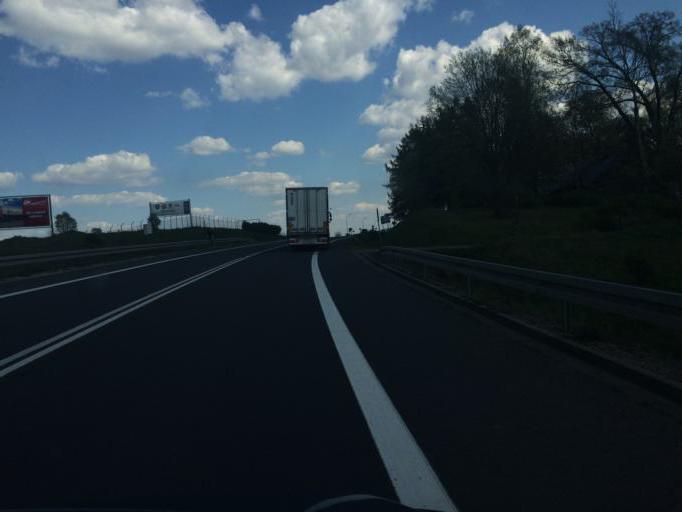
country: PL
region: Warmian-Masurian Voivodeship
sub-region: Olsztyn
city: Kortowo
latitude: 53.7703
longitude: 20.4054
